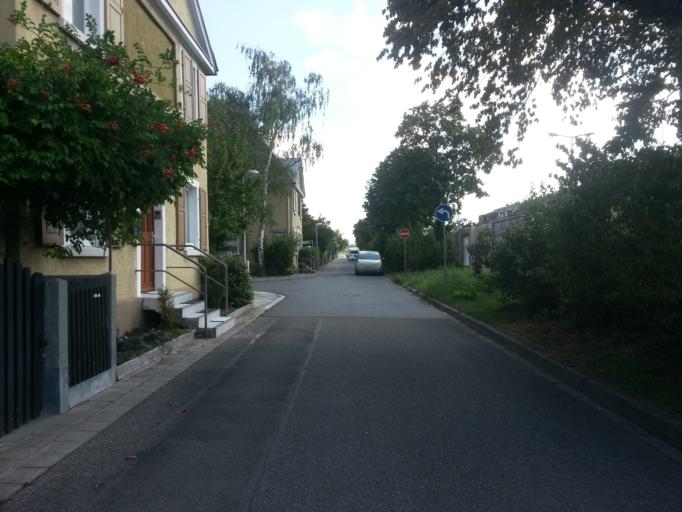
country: DE
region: Baden-Wuerttemberg
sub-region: Karlsruhe Region
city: Mannheim
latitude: 49.5270
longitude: 8.4940
